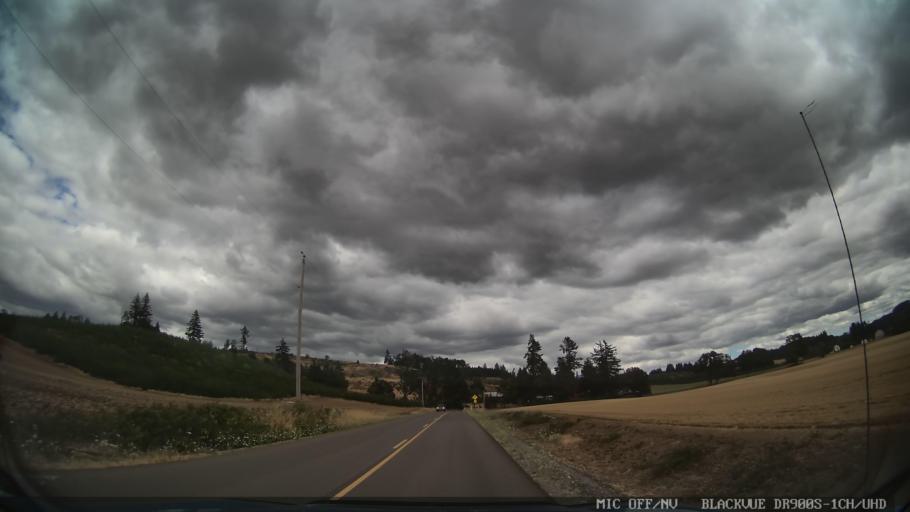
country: US
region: Oregon
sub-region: Marion County
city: Sublimity
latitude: 44.8725
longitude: -122.7106
